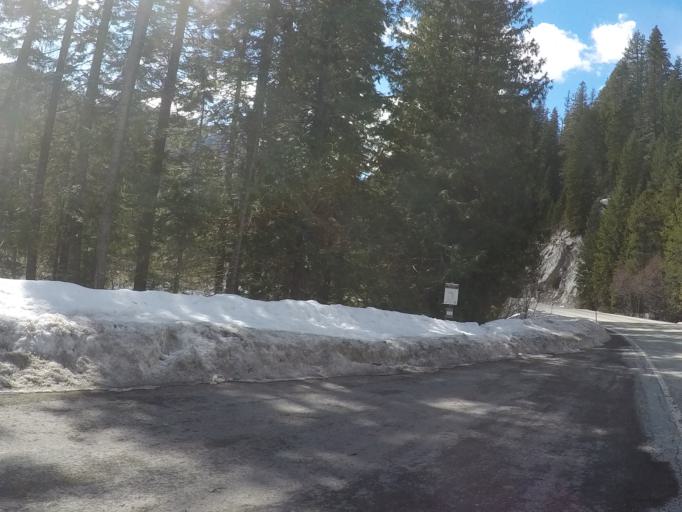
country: US
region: Montana
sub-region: Mineral County
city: Superior
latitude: 46.4776
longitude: -114.8823
